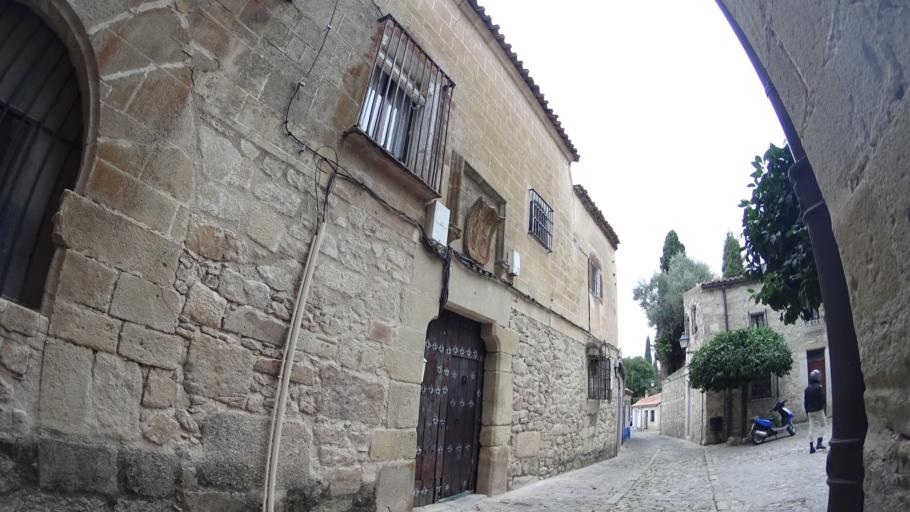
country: ES
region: Extremadura
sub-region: Provincia de Caceres
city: Trujillo
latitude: 39.4602
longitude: -5.8848
